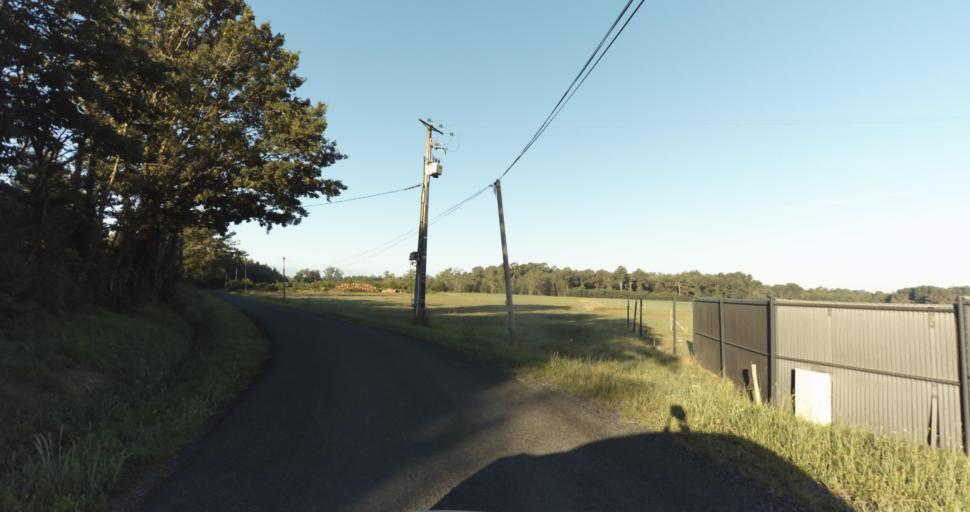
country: FR
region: Aquitaine
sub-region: Departement de la Gironde
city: Bazas
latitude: 44.4171
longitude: -0.2407
